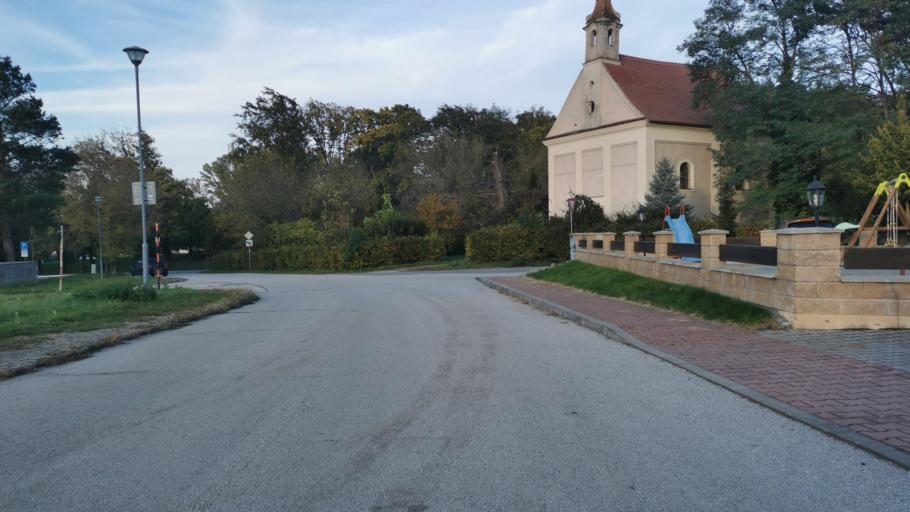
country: SK
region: Trnavsky
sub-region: Okres Skalica
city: Skalica
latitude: 48.8361
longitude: 17.2315
